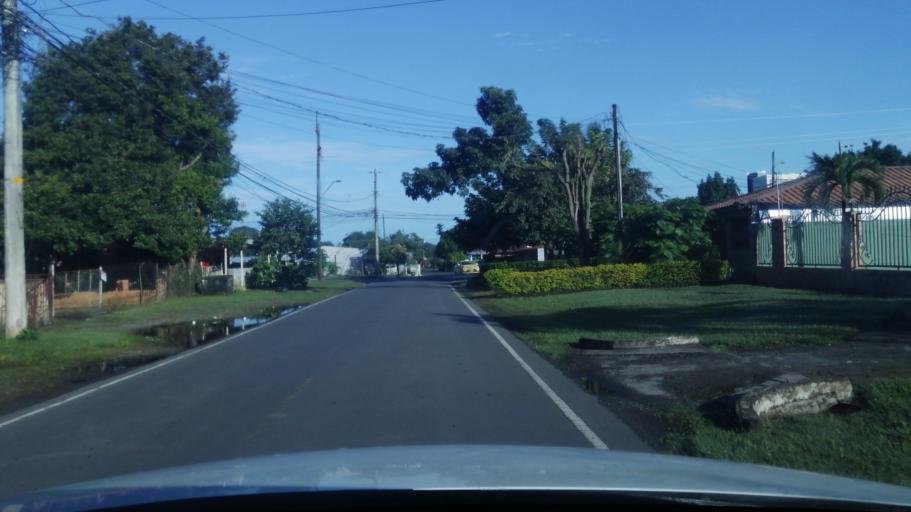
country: PA
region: Chiriqui
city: David
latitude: 8.4247
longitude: -82.4366
